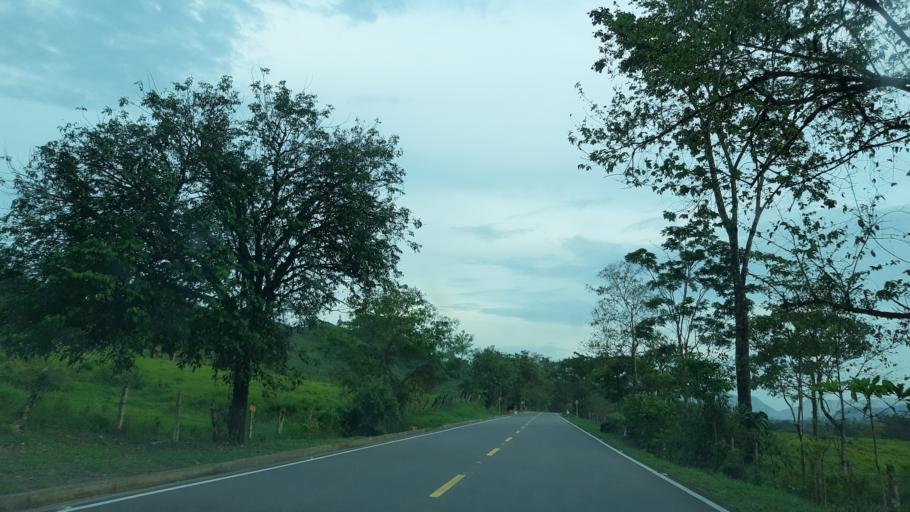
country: CO
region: Casanare
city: Sabanalarga
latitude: 4.7855
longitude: -73.0516
